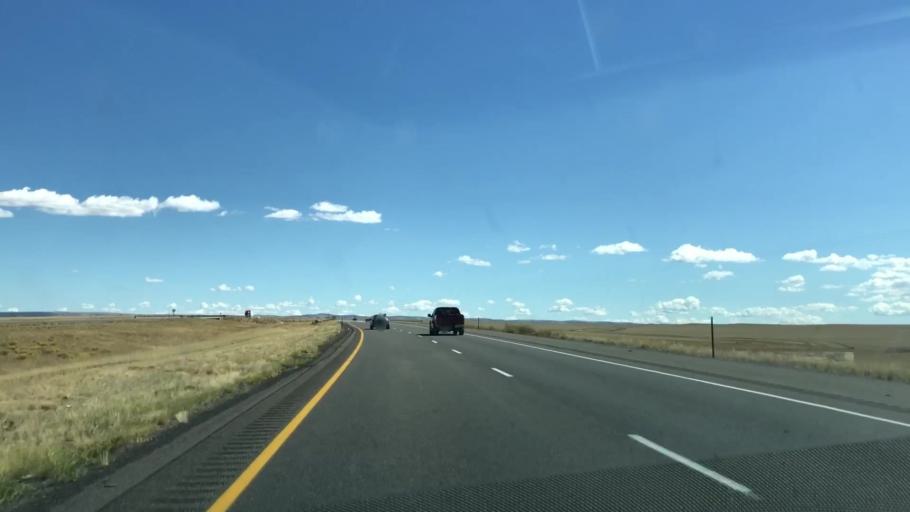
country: US
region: Wyoming
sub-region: Albany County
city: Laramie
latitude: 41.3550
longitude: -105.7453
